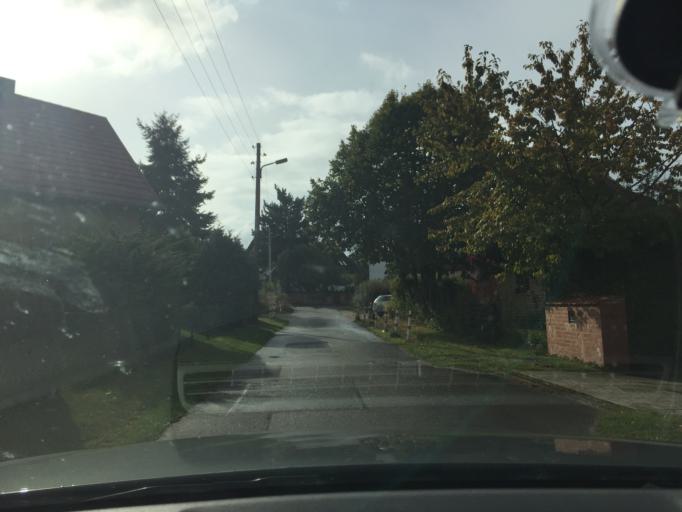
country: DE
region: Berlin
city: Hellersdorf
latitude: 52.5282
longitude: 13.6330
